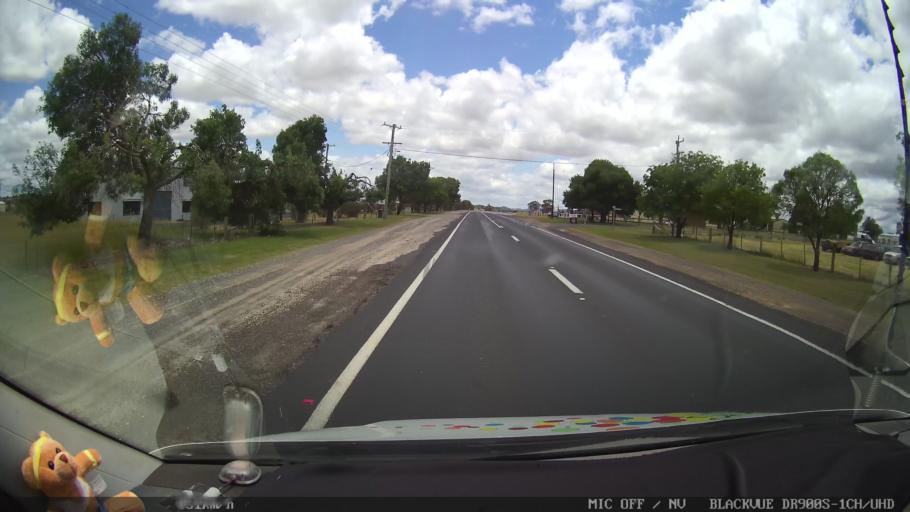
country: AU
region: New South Wales
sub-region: Glen Innes Severn
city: Glen Innes
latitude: -29.4373
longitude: 151.8470
